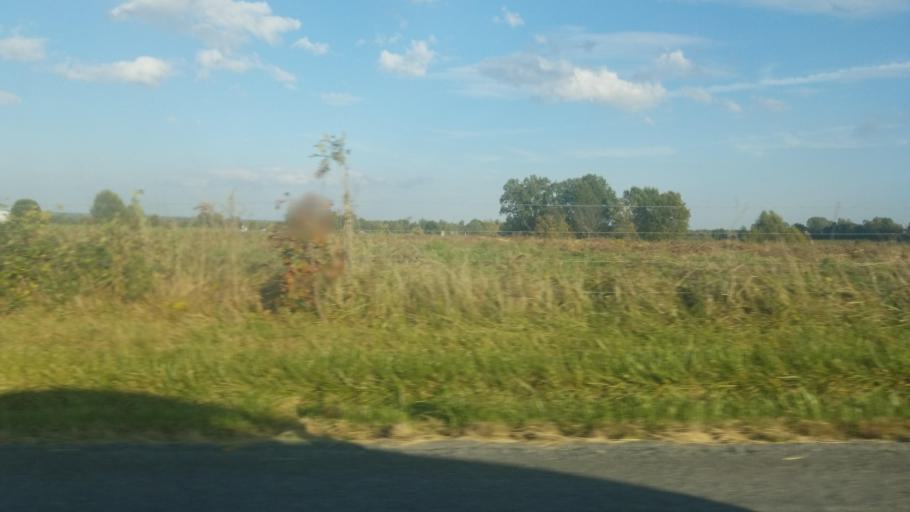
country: US
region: Illinois
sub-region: Saline County
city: Carrier Mills
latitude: 37.8027
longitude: -88.7119
